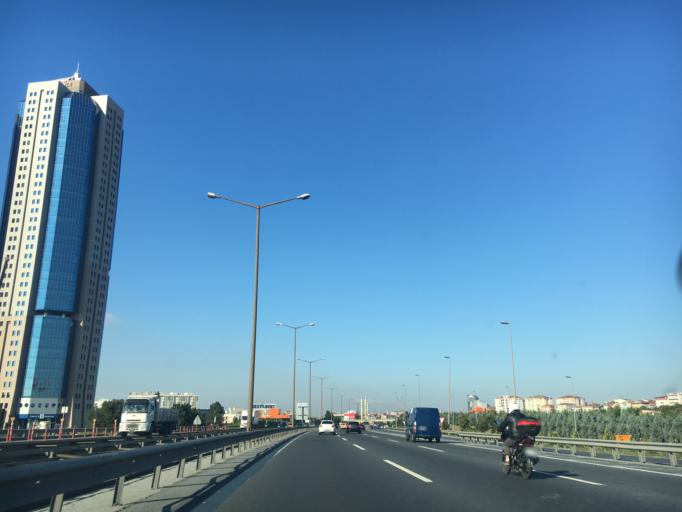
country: TR
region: Istanbul
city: Esenler
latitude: 41.0712
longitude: 28.8659
